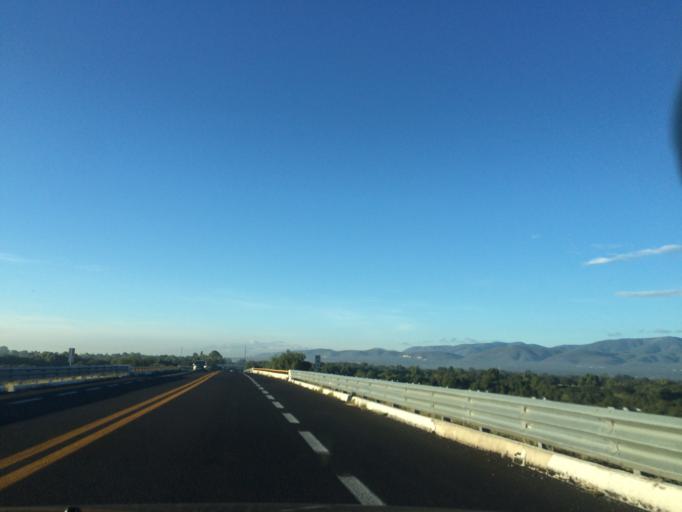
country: MX
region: Puebla
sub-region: Tehuacan
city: Magdalena Cuayucatepec
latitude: 18.5465
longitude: -97.4619
